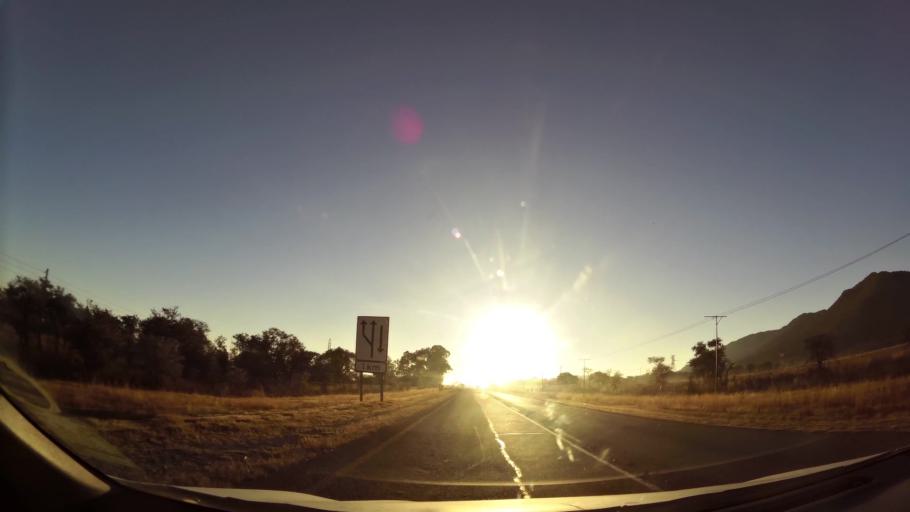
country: ZA
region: Limpopo
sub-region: Capricorn District Municipality
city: Polokwane
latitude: -24.0218
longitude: 29.3042
